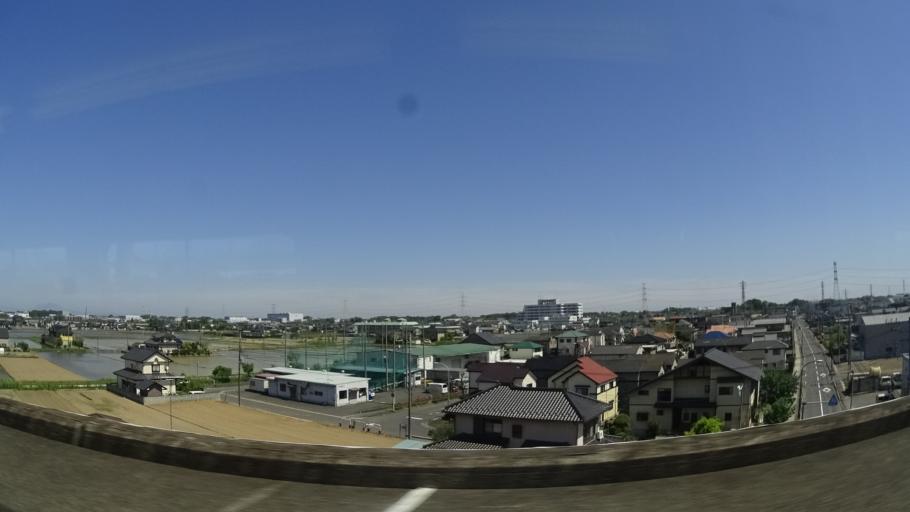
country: JP
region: Saitama
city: Kurihashi
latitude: 36.1190
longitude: 139.7114
